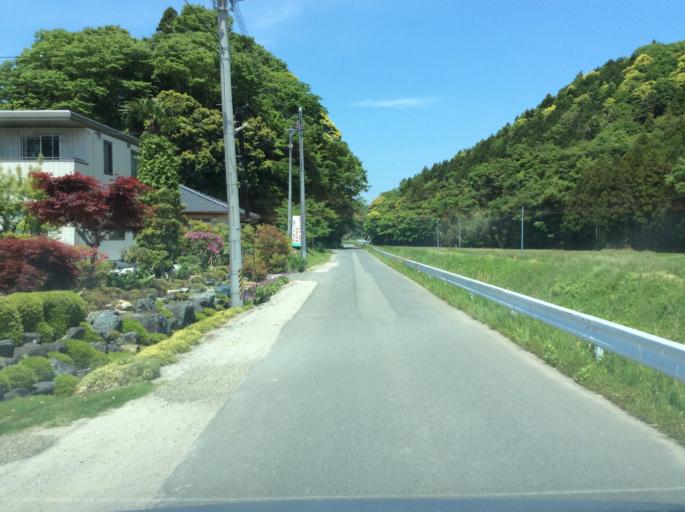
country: JP
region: Fukushima
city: Iwaki
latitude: 37.0207
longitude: 140.9386
